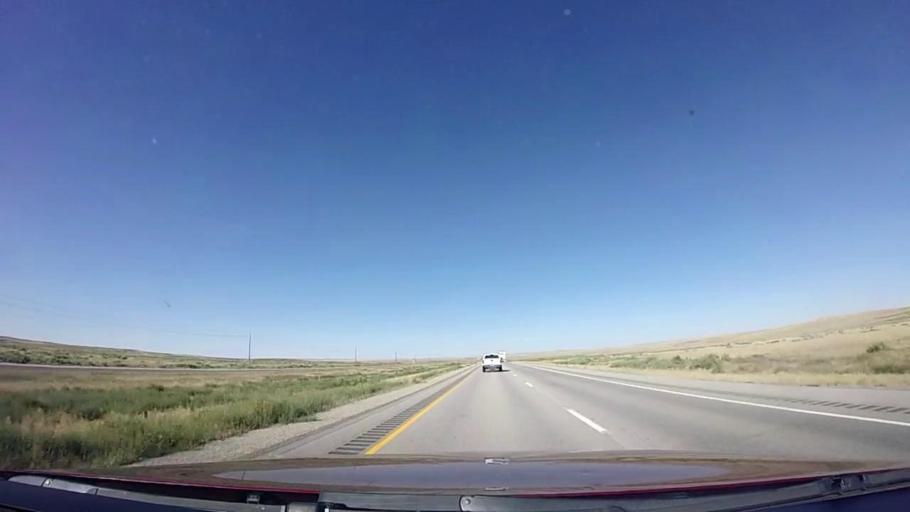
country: US
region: Wyoming
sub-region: Carbon County
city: Rawlins
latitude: 41.7832
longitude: -107.4219
